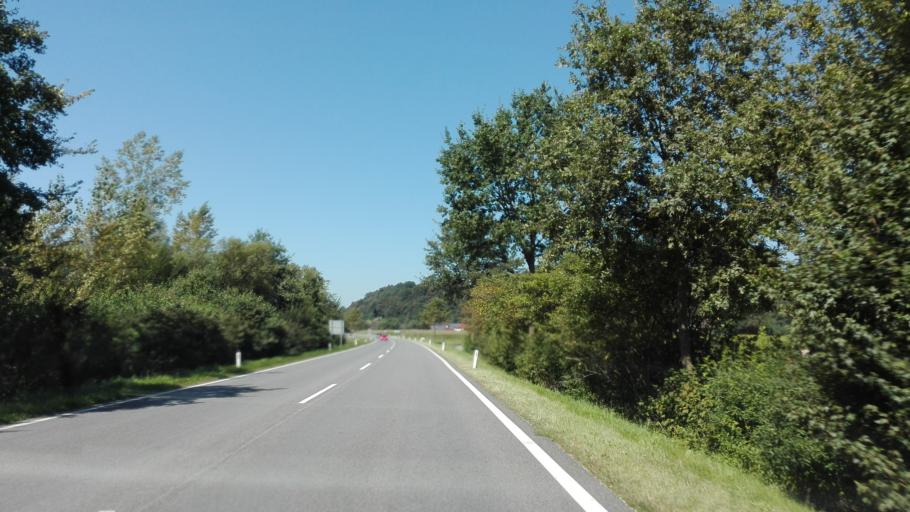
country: AT
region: Upper Austria
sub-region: Politischer Bezirk Perg
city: Bad Kreuzen
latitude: 48.2215
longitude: 14.7307
